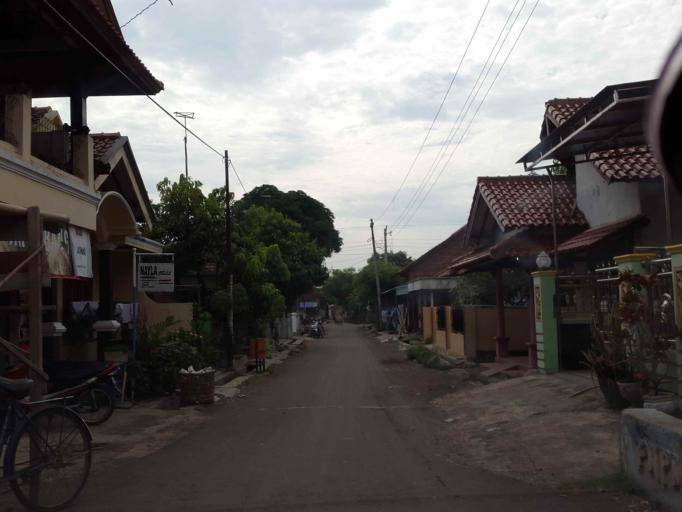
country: ID
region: Central Java
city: Dukuhturi
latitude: -6.8709
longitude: 109.0560
